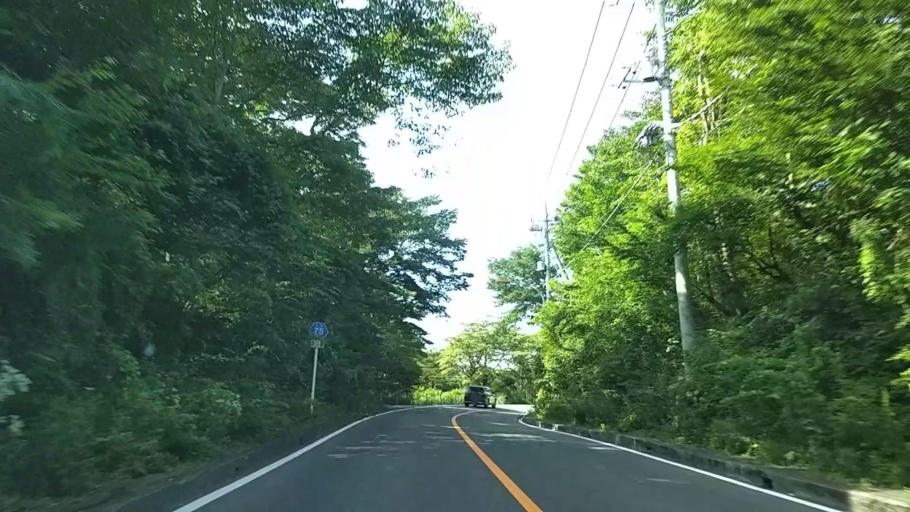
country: JP
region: Kanagawa
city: Hakone
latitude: 35.2182
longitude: 139.0057
